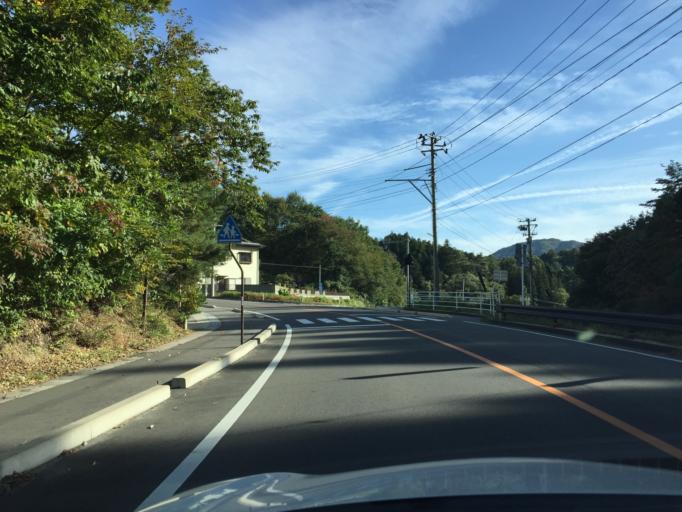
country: JP
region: Fukushima
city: Miharu
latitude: 37.3585
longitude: 140.5141
